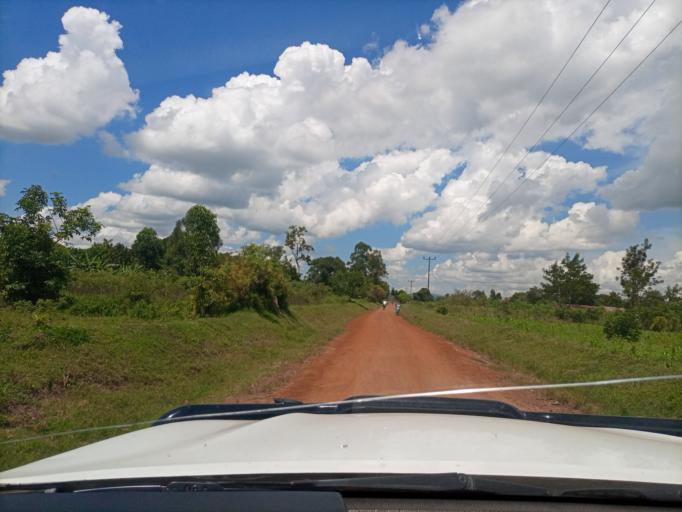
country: UG
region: Eastern Region
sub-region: Tororo District
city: Tororo
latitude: 0.6502
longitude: 33.9972
